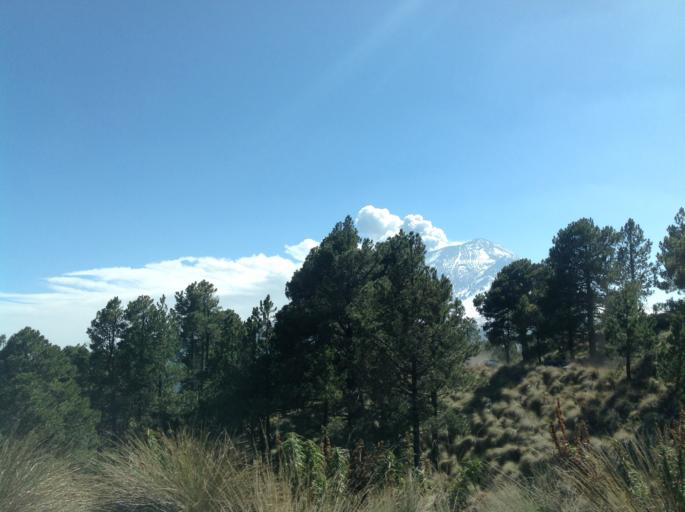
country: MX
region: Mexico
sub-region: Amecameca
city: San Diego Huehuecalco
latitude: 19.1082
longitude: -98.6455
